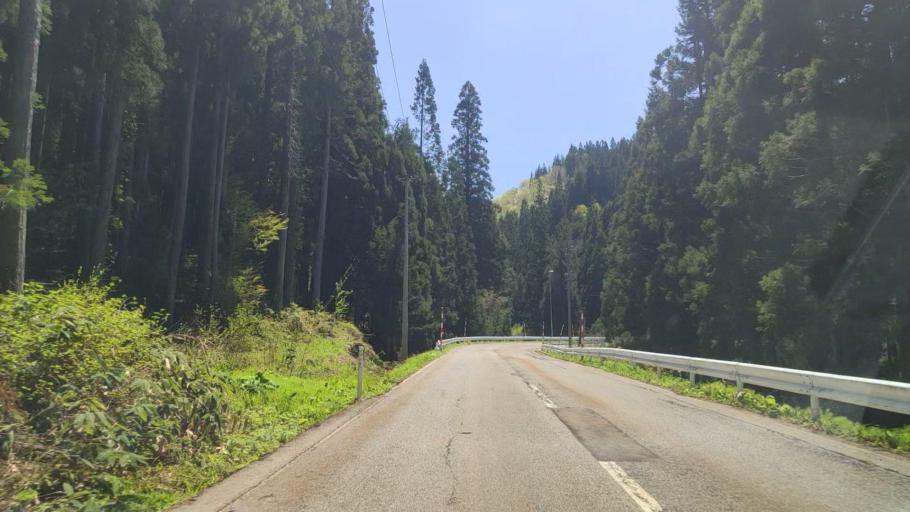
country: JP
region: Yamagata
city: Shinjo
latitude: 38.9749
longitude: 140.3576
